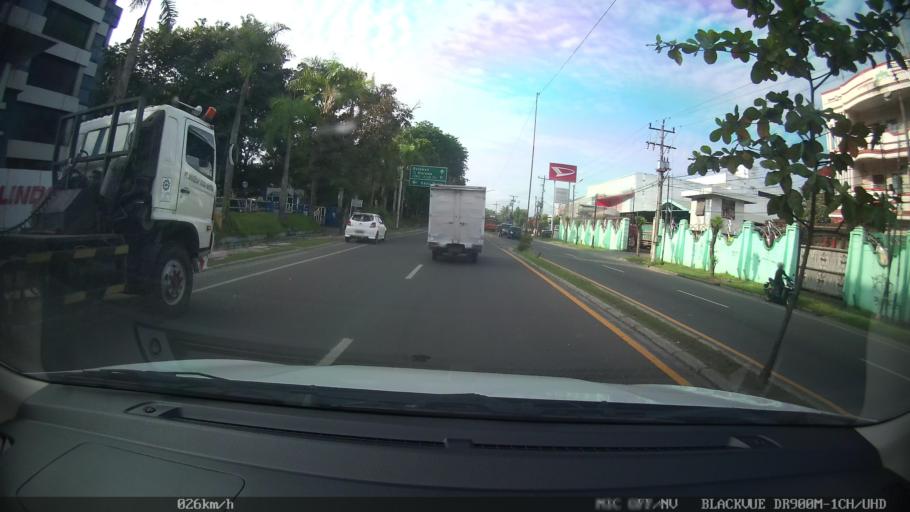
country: ID
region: North Sumatra
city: Medan
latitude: 3.6405
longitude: 98.6810
